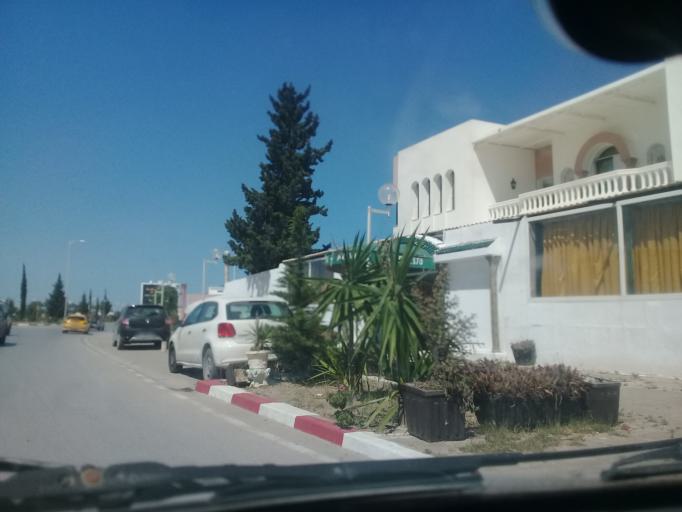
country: TN
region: Ariana
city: Ariana
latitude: 36.8401
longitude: 10.2475
